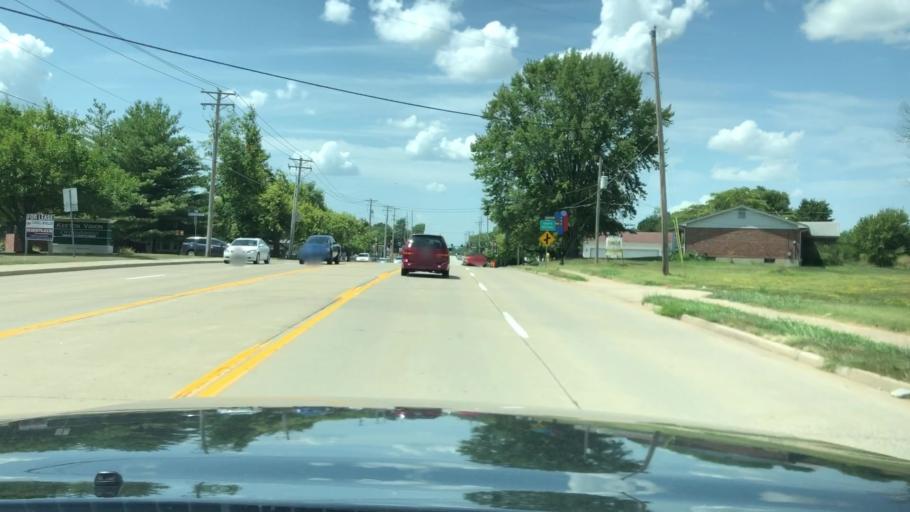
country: US
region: Missouri
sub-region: Saint Charles County
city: Saint Peters
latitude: 38.7911
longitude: -90.6034
